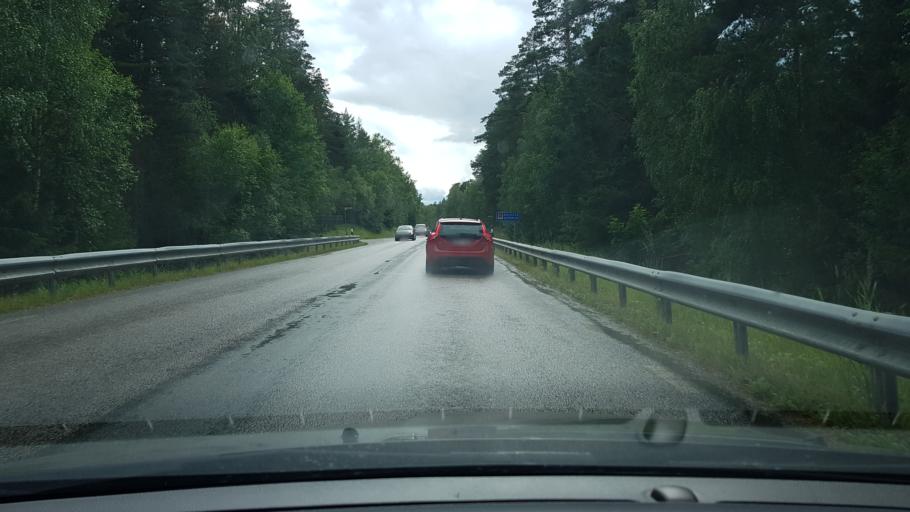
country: SE
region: Uppsala
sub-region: Uppsala Kommun
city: Saevja
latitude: 59.7934
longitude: 17.6758
